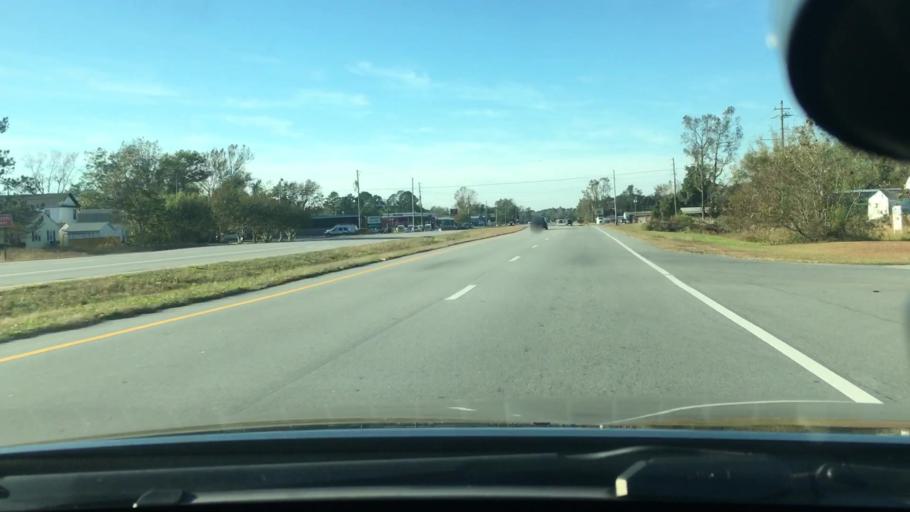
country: US
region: North Carolina
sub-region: Craven County
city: New Bern
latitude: 35.1201
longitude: -77.0172
